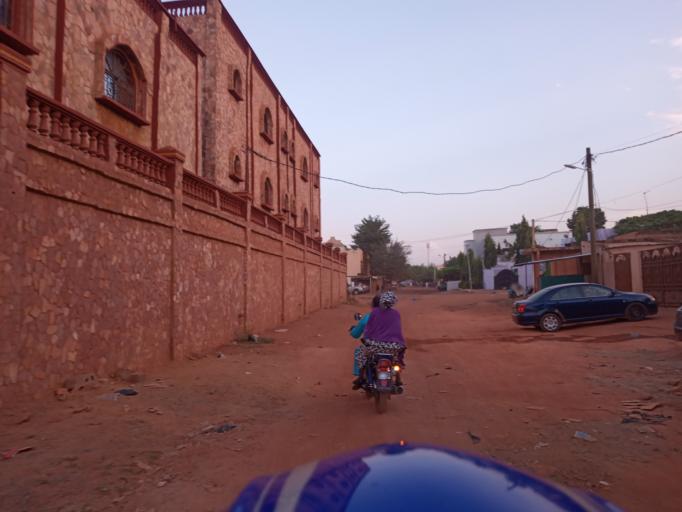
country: ML
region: Bamako
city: Bamako
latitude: 12.5702
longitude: -7.9856
